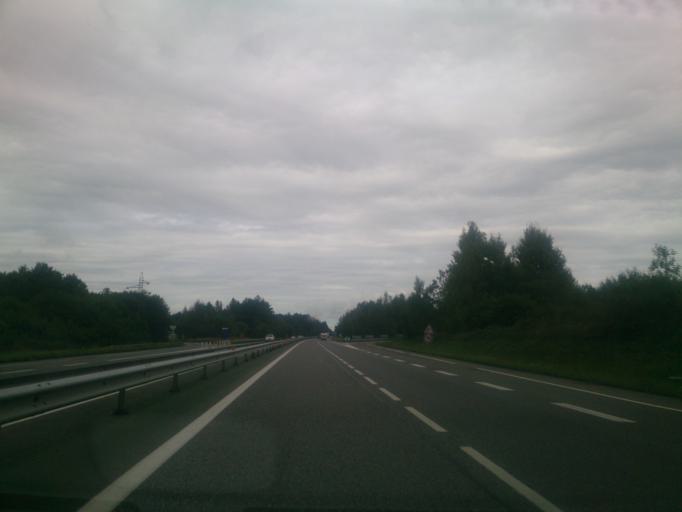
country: FR
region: Midi-Pyrenees
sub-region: Departement de la Haute-Garonne
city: Montrejeau
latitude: 43.1031
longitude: 0.4777
